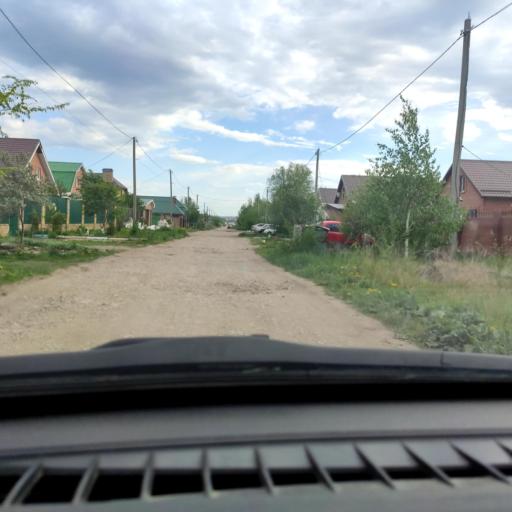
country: RU
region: Samara
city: Tol'yatti
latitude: 53.5738
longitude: 49.4117
